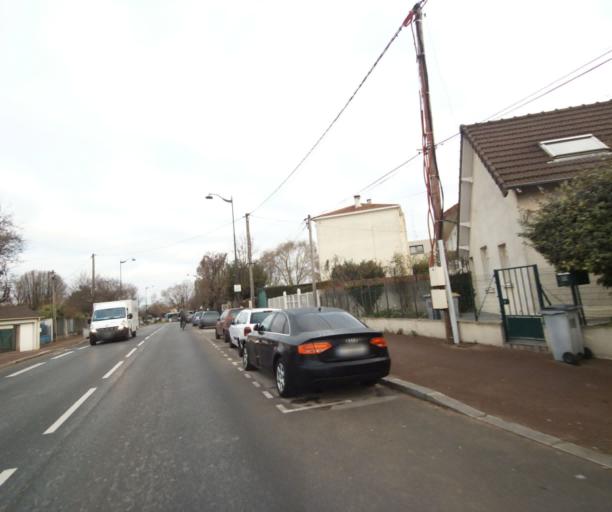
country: FR
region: Ile-de-France
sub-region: Departement des Hauts-de-Seine
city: Rueil-Malmaison
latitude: 48.8751
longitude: 2.2010
